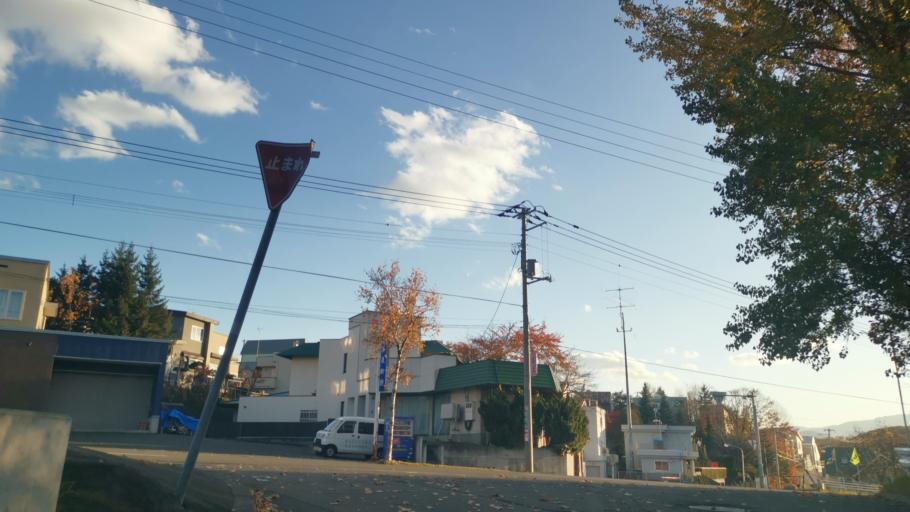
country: JP
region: Hokkaido
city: Sapporo
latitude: 42.9997
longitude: 141.3667
